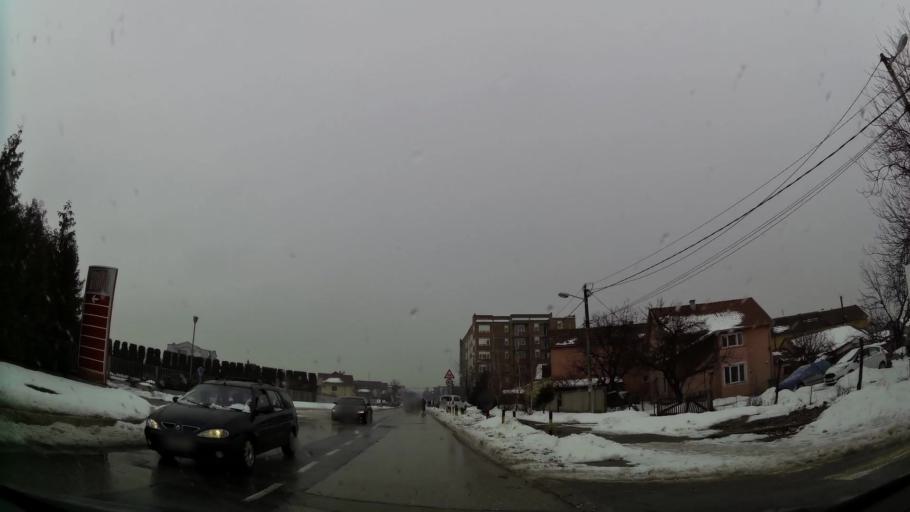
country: RS
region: Central Serbia
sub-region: Belgrade
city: Zemun
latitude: 44.8465
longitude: 20.3605
